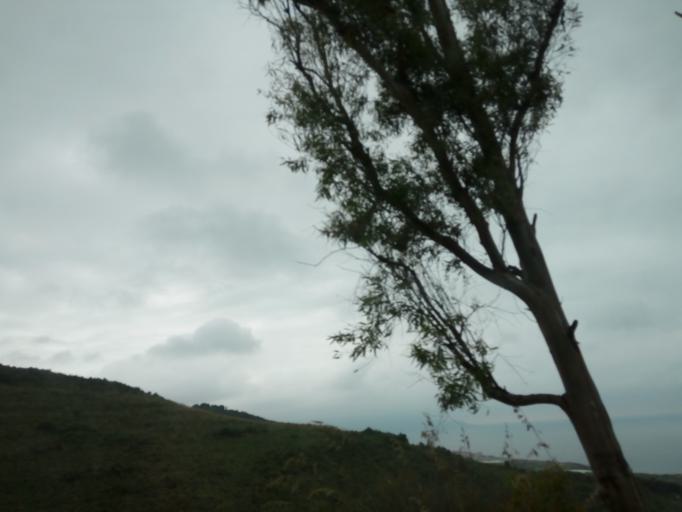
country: DZ
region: Tipaza
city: Tipasa
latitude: 36.5838
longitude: 2.5420
